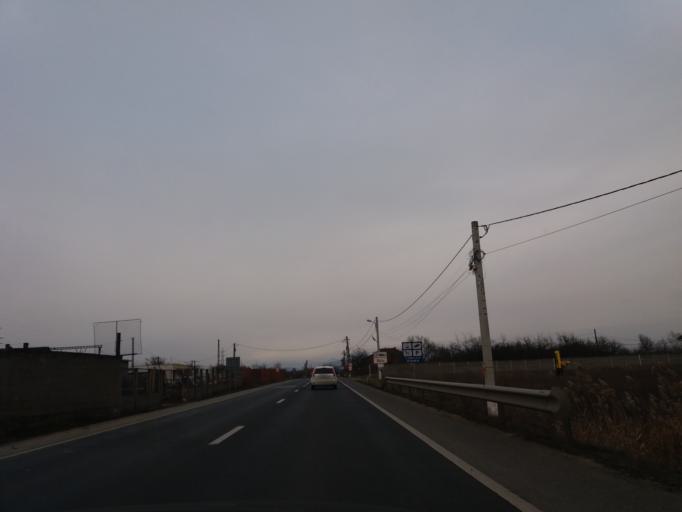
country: RO
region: Hunedoara
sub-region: Comuna Bacia
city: Bacia
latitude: 45.7944
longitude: 23.0015
